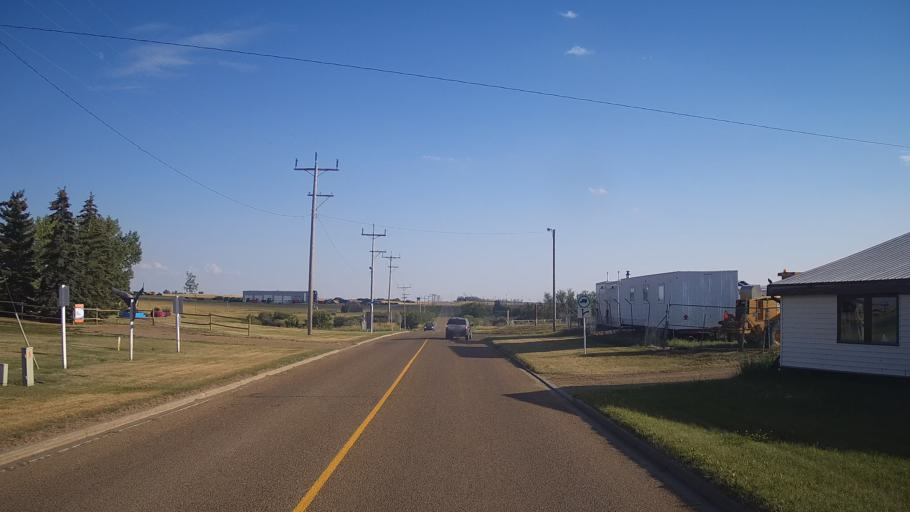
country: CA
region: Alberta
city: Hanna
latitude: 51.6436
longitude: -111.9185
